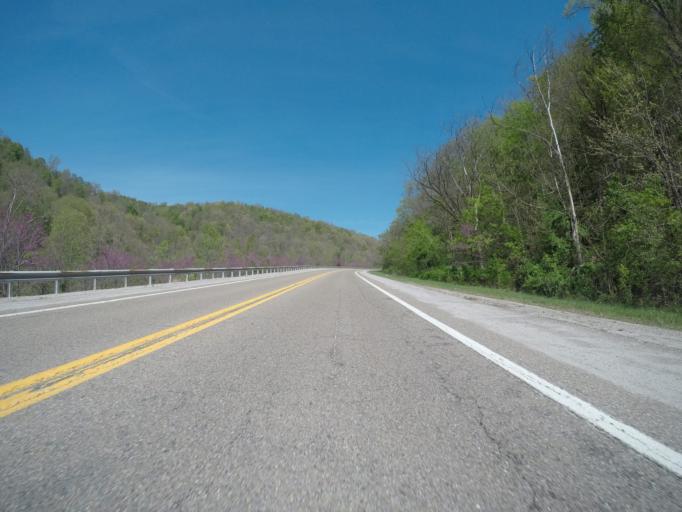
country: US
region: West Virginia
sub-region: Kanawha County
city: Charleston
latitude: 38.4130
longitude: -81.6400
